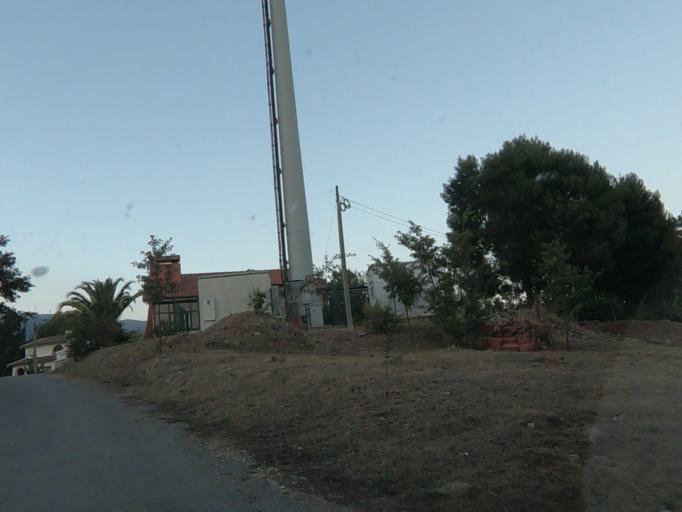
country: PT
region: Vila Real
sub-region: Vila Real
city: Vila Real
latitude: 41.3092
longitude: -7.7645
